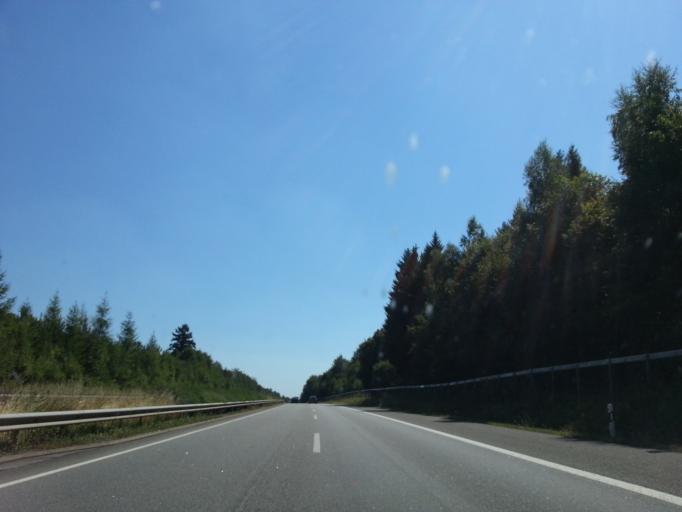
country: DE
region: Rheinland-Pfalz
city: Bergweiler
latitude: 49.9795
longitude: 6.8045
